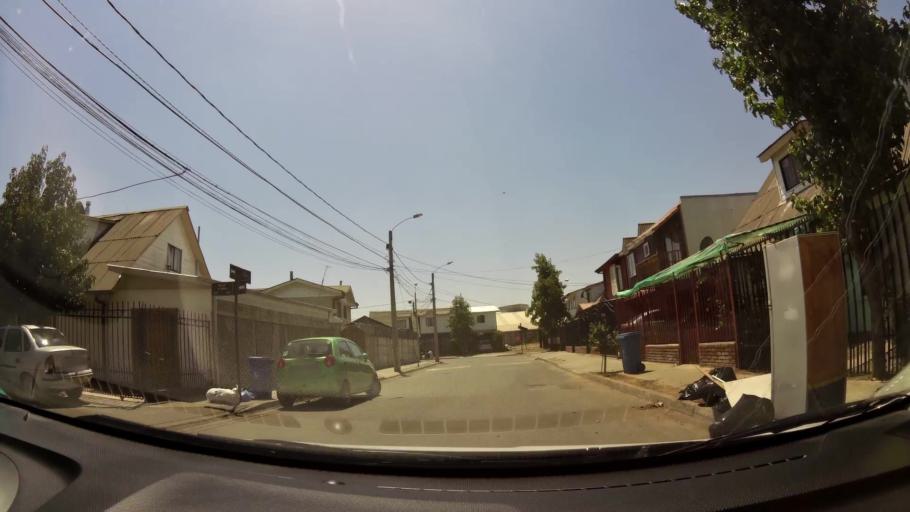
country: CL
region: Maule
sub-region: Provincia de Talca
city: Talca
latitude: -35.4349
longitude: -71.6324
